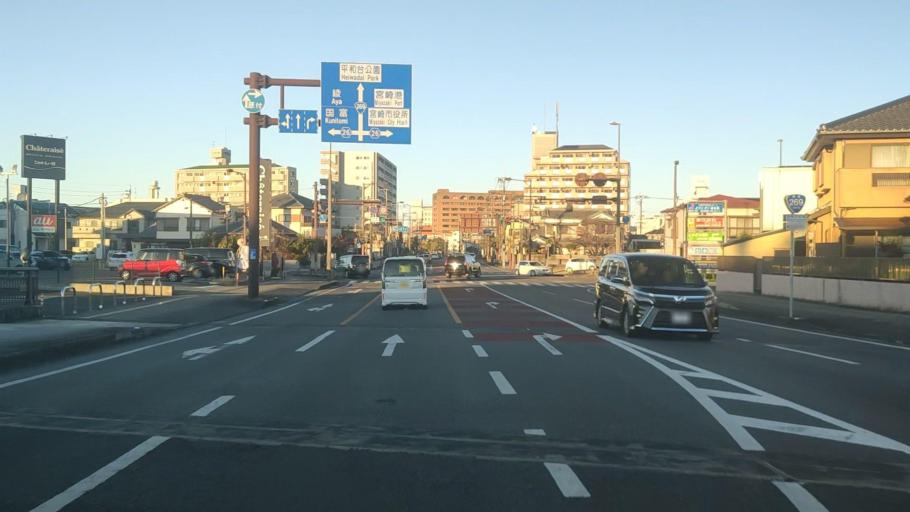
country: JP
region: Miyazaki
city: Miyazaki-shi
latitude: 31.9118
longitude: 131.4136
